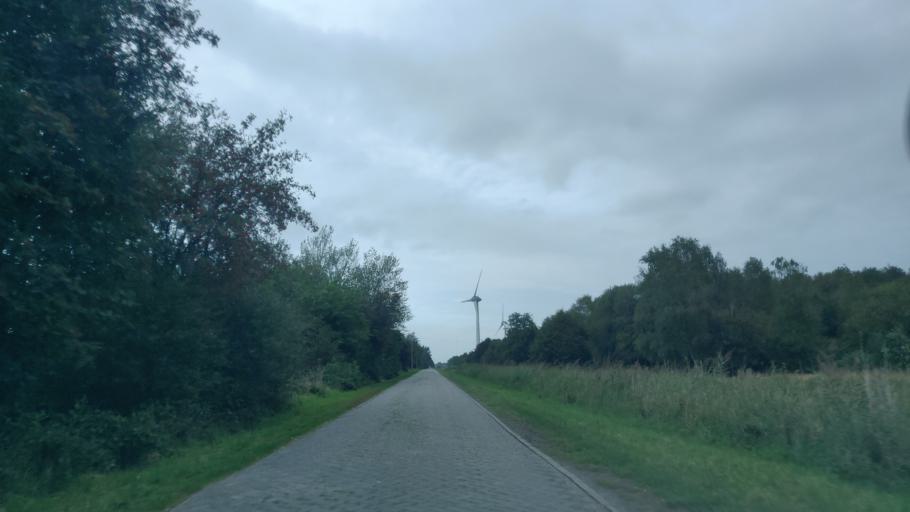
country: DE
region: Lower Saxony
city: Aurich
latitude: 53.4889
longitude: 7.4123
